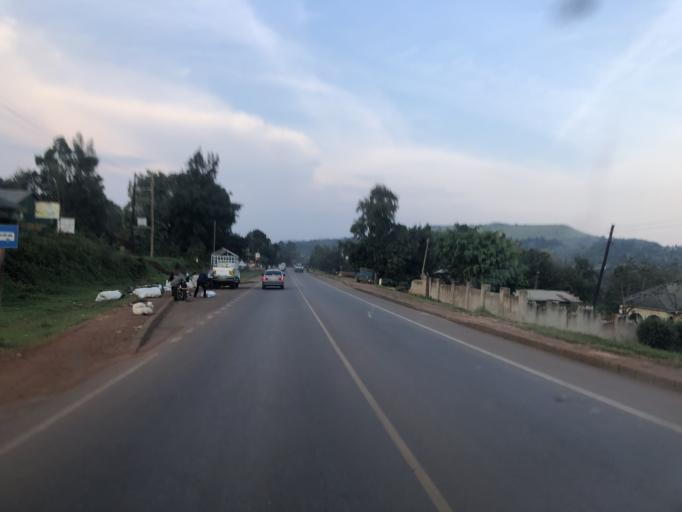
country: UG
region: Central Region
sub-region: Mpigi District
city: Mpigi
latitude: 0.2219
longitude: 32.3361
